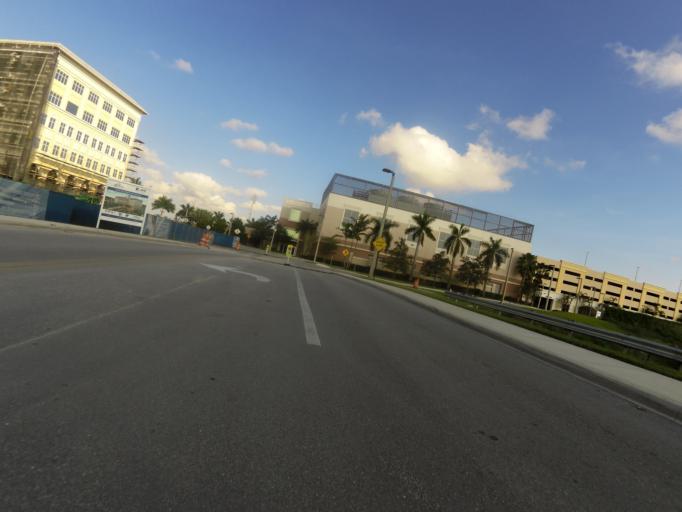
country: US
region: Florida
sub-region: Broward County
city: Davie
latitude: 26.0800
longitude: -80.2490
